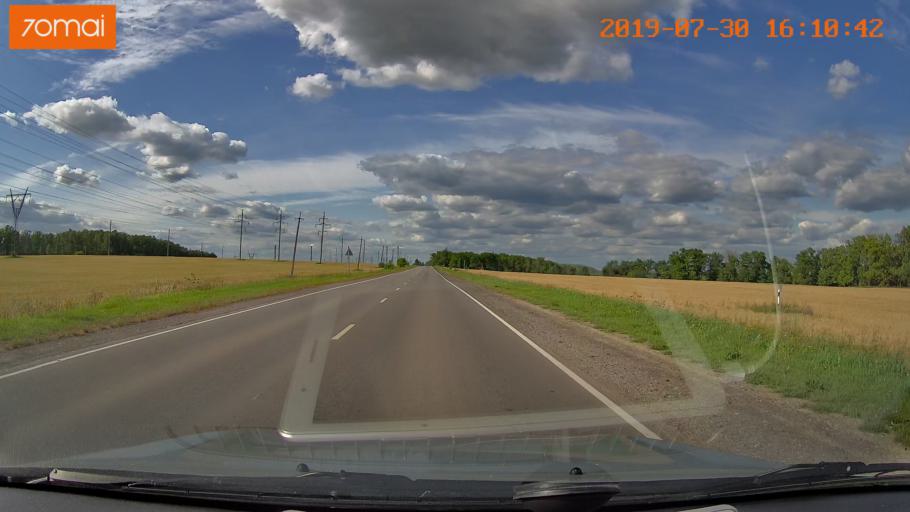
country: RU
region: Moskovskaya
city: Peski
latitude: 55.2655
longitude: 38.7149
